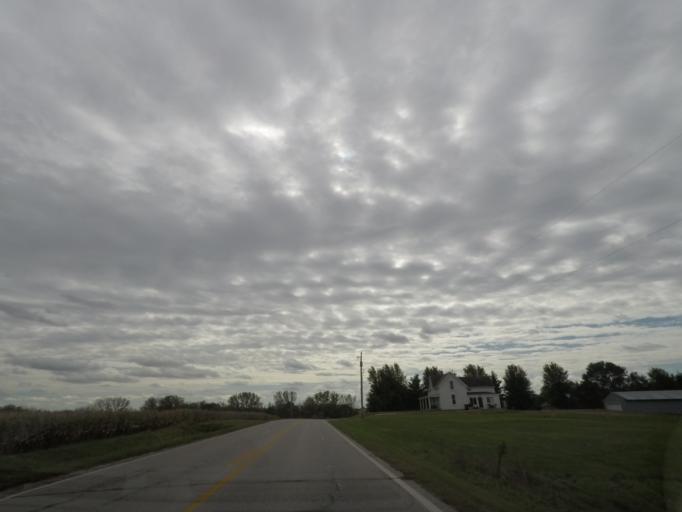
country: US
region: Iowa
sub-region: Story County
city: Huxley
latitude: 41.8398
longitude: -93.5315
